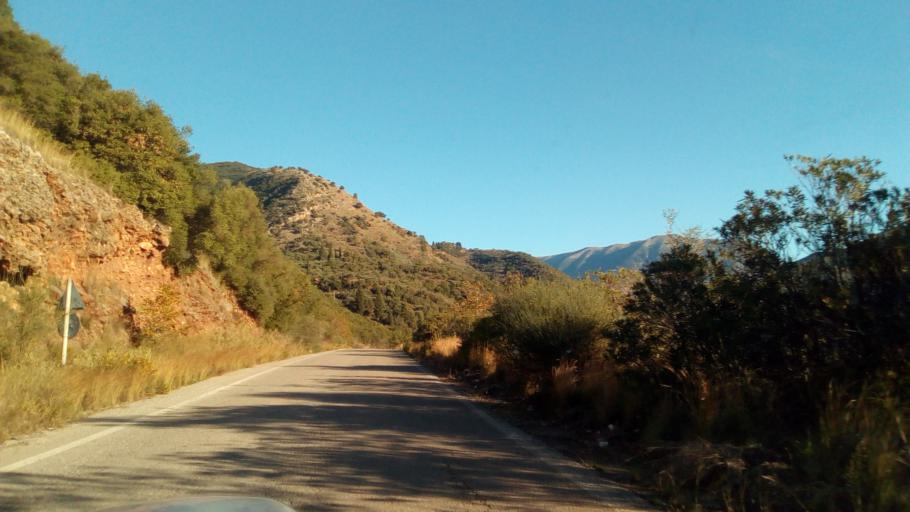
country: GR
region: West Greece
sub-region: Nomos Aitolias kai Akarnanias
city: Nafpaktos
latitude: 38.4294
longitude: 21.8775
